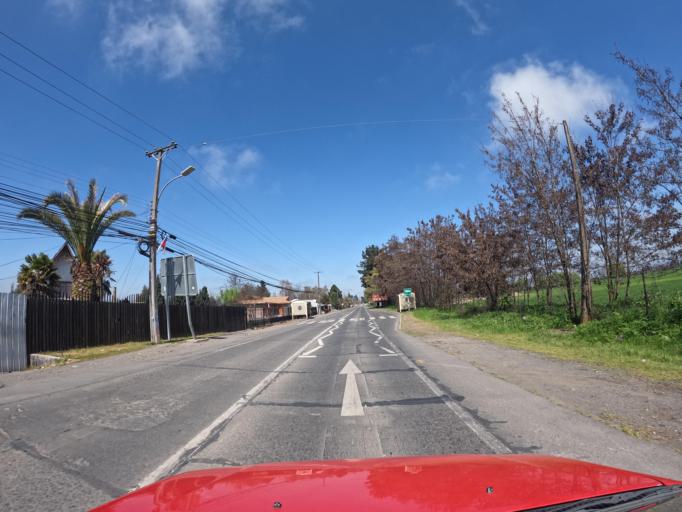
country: CL
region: Maule
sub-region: Provincia de Curico
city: Molina
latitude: -35.0689
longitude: -71.2554
